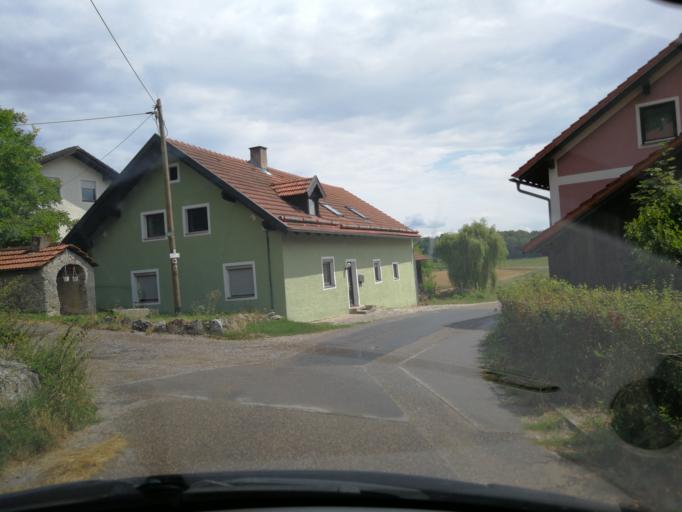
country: DE
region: Bavaria
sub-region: Upper Palatinate
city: Brennberg
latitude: 49.0710
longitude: 12.4021
